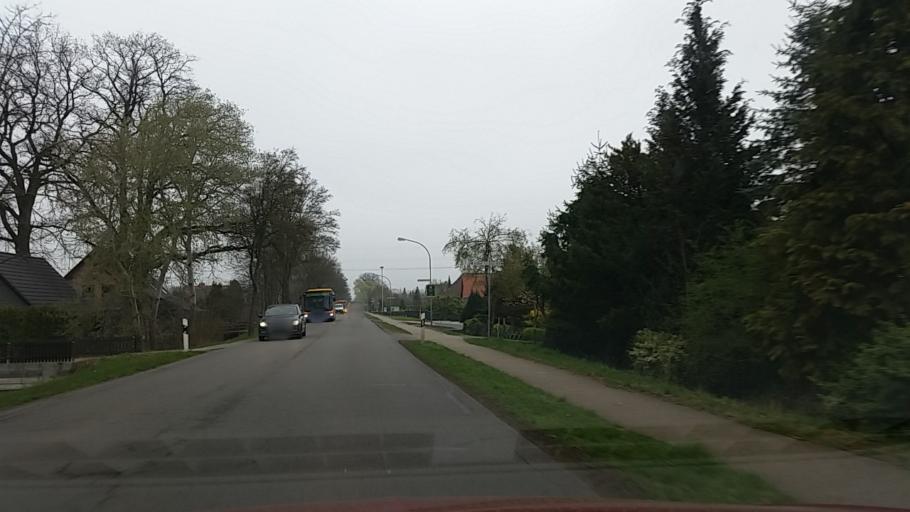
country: DE
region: Lower Saxony
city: Sassenburg
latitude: 52.5150
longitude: 10.5847
